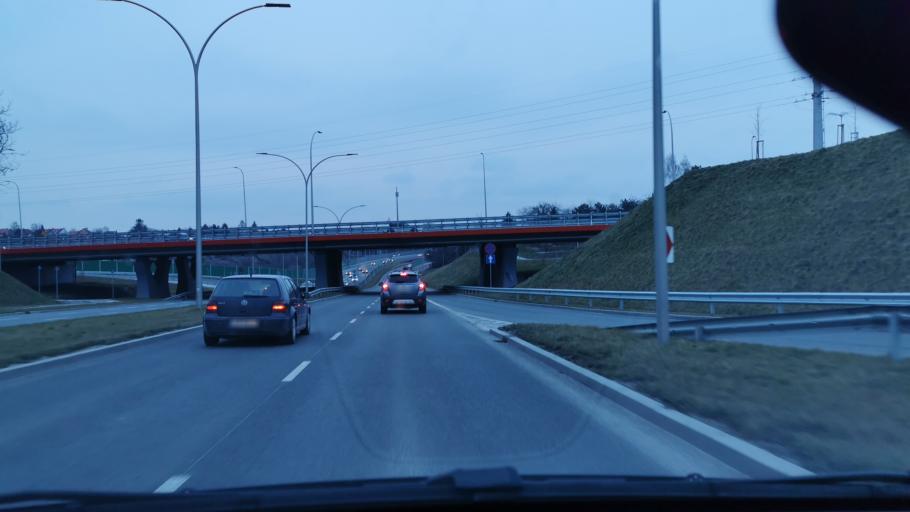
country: PL
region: Lublin Voivodeship
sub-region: Powiat lubelski
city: Lublin
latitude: 51.2512
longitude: 22.5048
